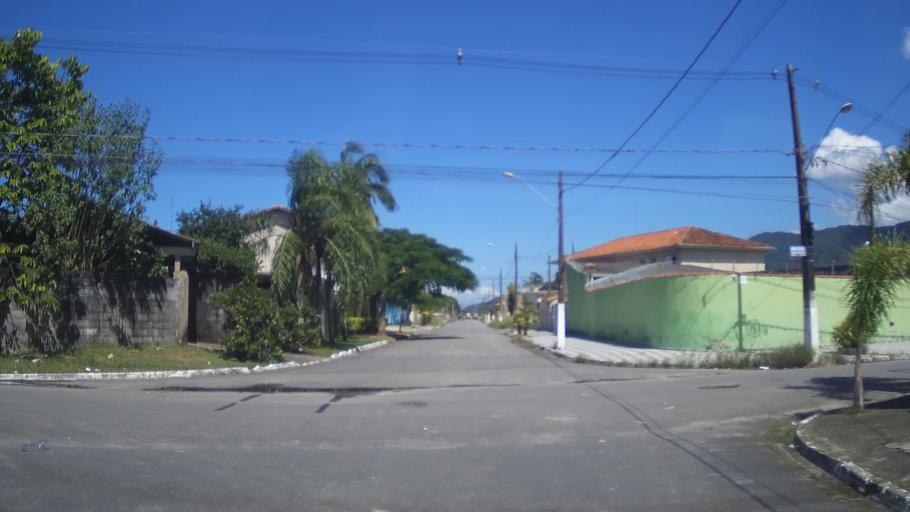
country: BR
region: Sao Paulo
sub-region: Mongagua
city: Mongagua
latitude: -24.0561
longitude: -46.5557
